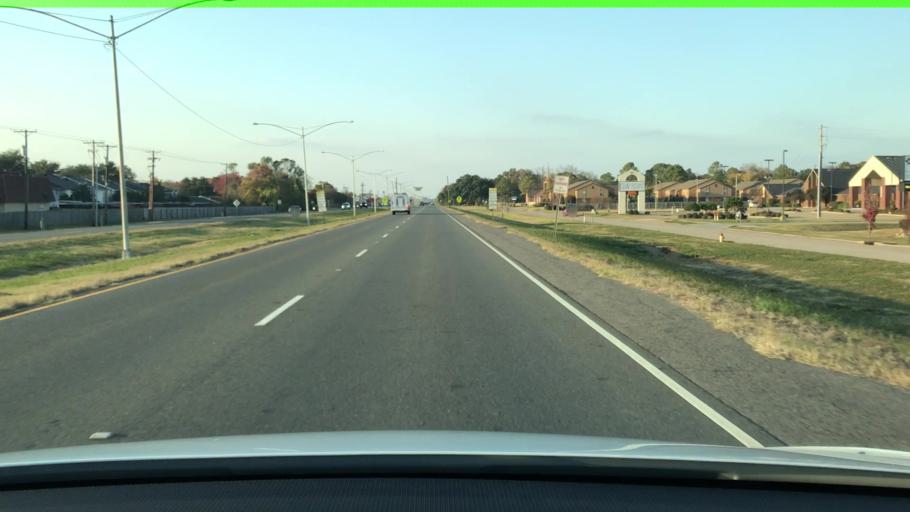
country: US
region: Louisiana
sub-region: Bossier Parish
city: Bossier City
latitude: 32.4142
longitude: -93.7015
